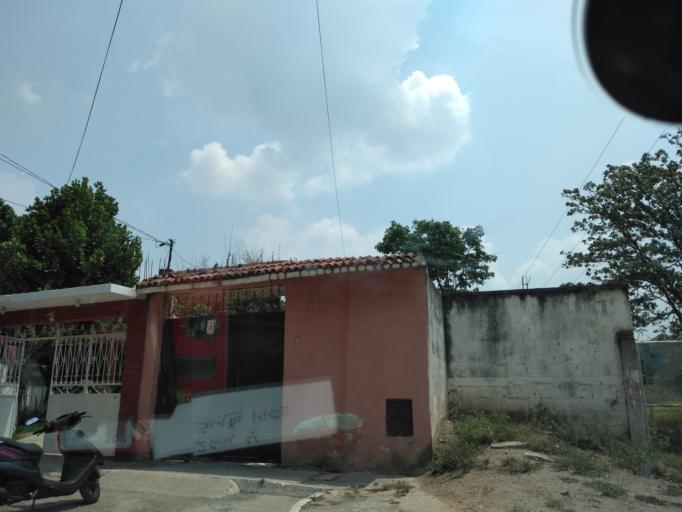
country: GT
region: Guatemala
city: Petapa
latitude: 14.5260
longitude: -90.5424
